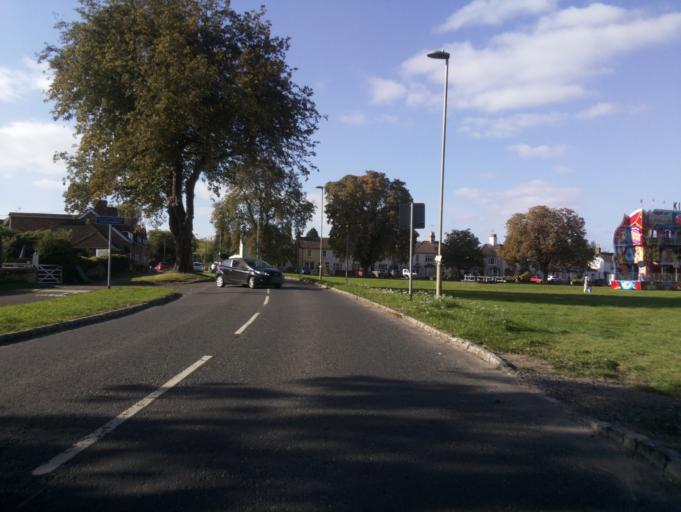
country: GB
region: England
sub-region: Hampshire
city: Alton
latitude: 51.1410
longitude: -0.9844
